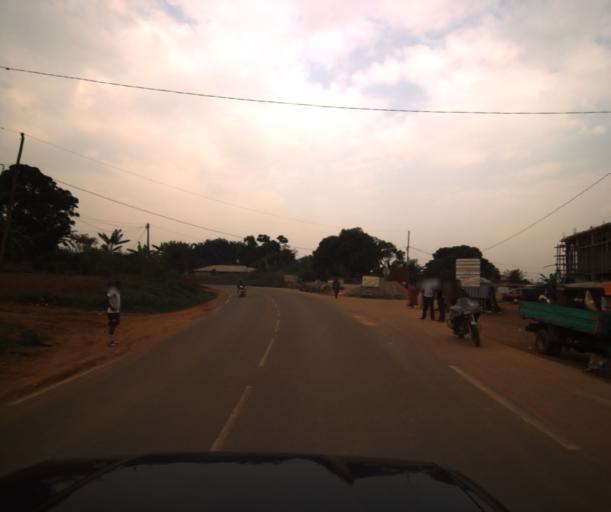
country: CM
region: Centre
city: Mbankomo
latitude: 3.8022
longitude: 11.4632
